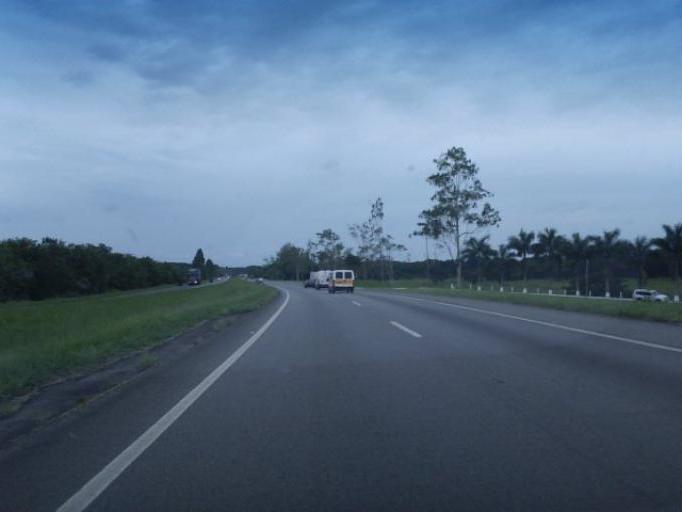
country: BR
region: Sao Paulo
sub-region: Registro
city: Registro
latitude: -24.5842
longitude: -47.8841
